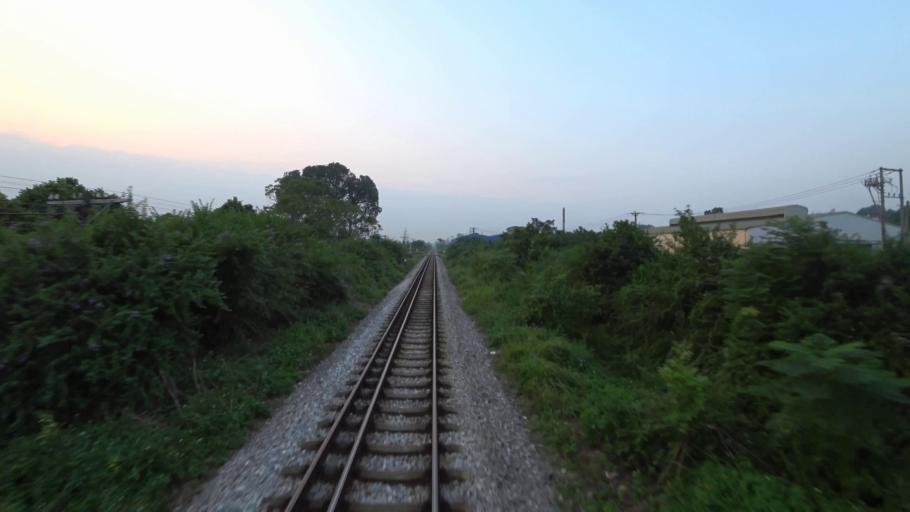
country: VN
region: Ha Noi
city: Dong Anh
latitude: 21.1450
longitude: 105.8614
